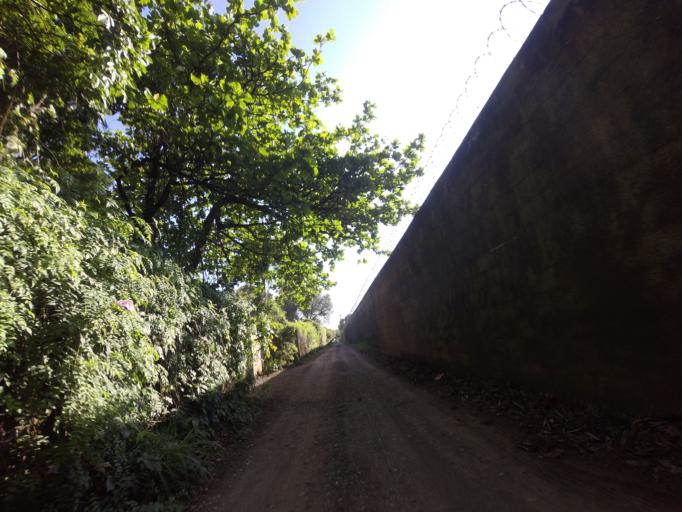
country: BR
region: Sao Paulo
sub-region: Piracicaba
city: Piracicaba
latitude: -22.7350
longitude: -47.5985
